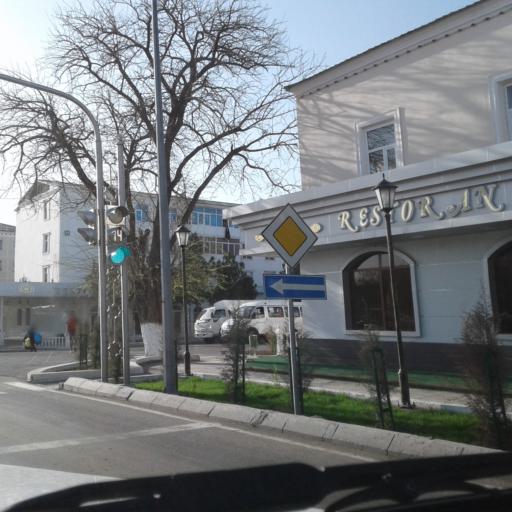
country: TM
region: Lebap
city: Turkmenabat
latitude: 39.0942
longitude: 63.5746
